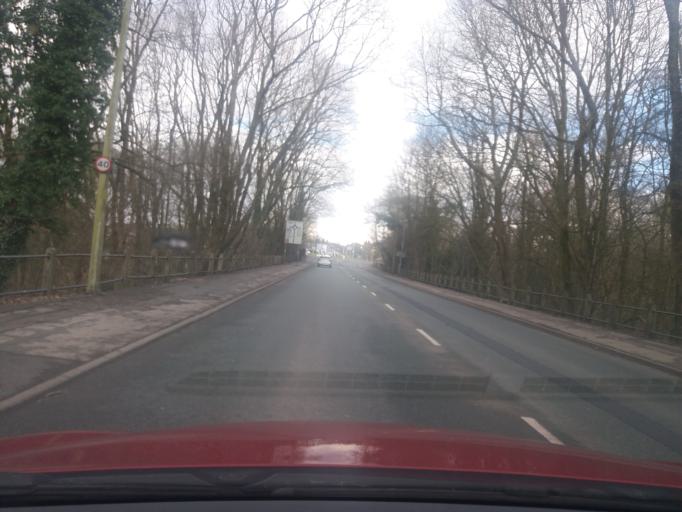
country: GB
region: England
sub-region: Lancashire
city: Coppull
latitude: 53.6370
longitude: -2.6508
